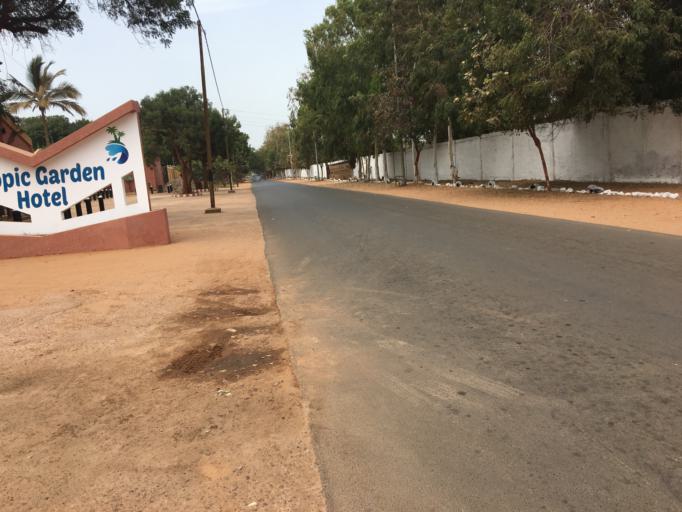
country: GM
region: Banjul
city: Bakau
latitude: 13.4784
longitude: -16.6830
